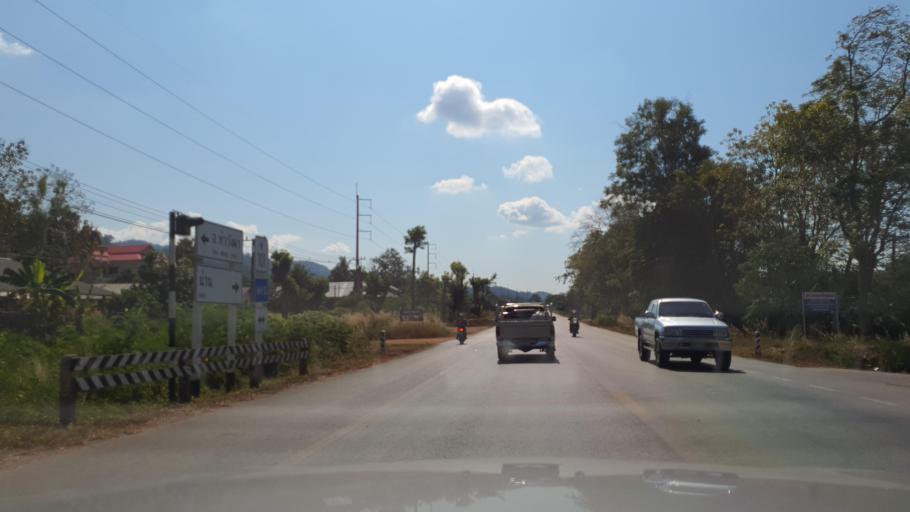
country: TH
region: Nan
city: Tha Wang Pha
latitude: 19.0514
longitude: 100.8068
